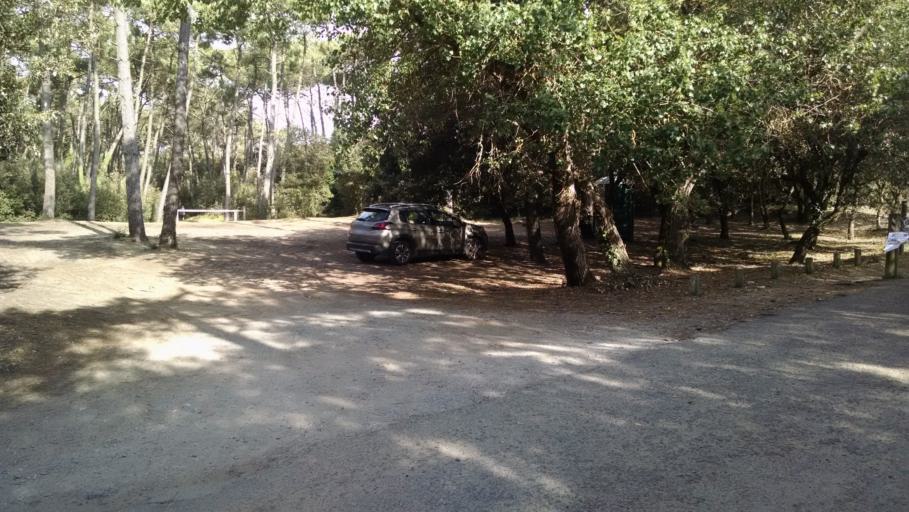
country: FR
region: Pays de la Loire
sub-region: Departement de la Vendee
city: Jard-sur-Mer
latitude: 46.4067
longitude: -1.5520
